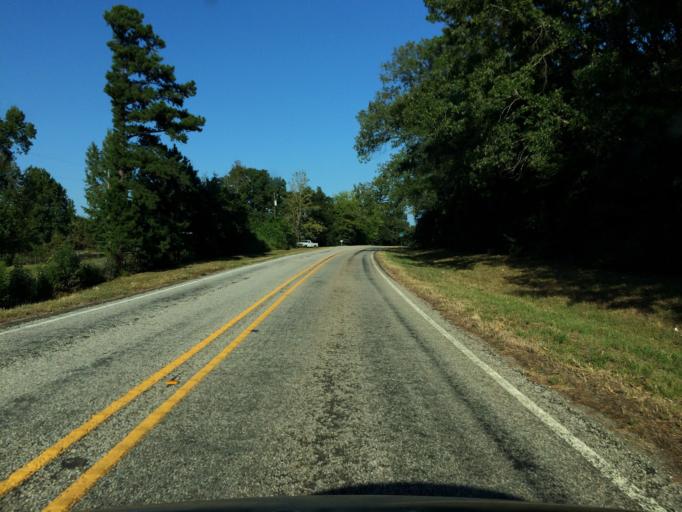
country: US
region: Texas
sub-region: Wood County
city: Hawkins
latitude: 32.6469
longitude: -95.2422
